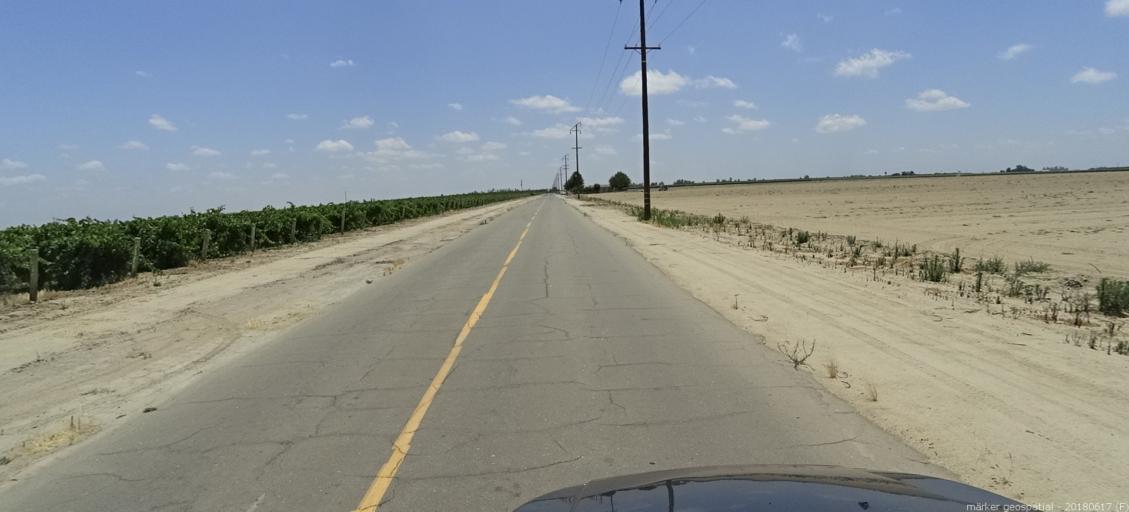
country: US
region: California
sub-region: Fresno County
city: Biola
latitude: 36.8329
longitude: -120.1150
